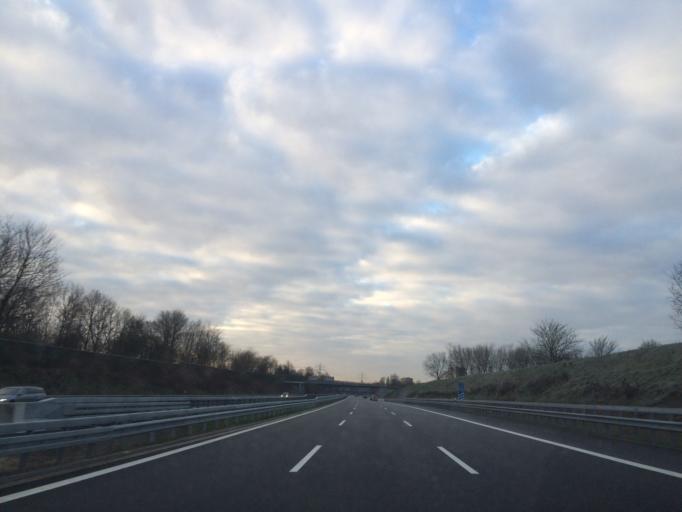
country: DE
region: Schleswig-Holstein
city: Oststeinbek
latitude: 53.5515
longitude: 10.1500
